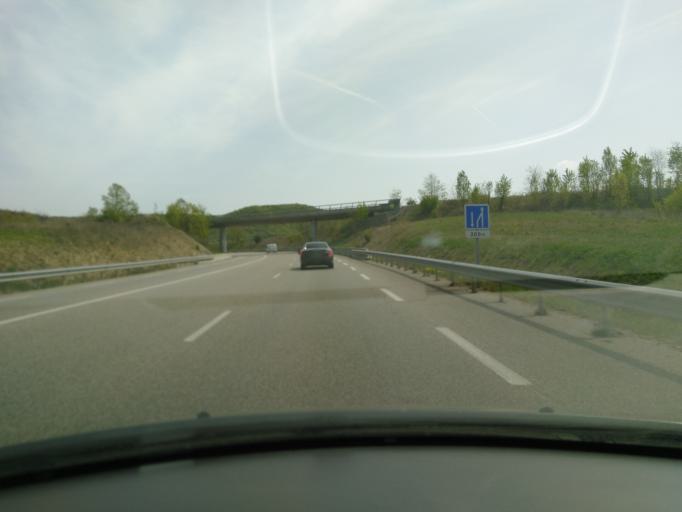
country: FR
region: Rhone-Alpes
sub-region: Departement de l'Ardeche
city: Lavilledieu
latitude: 44.5641
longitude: 4.4660
